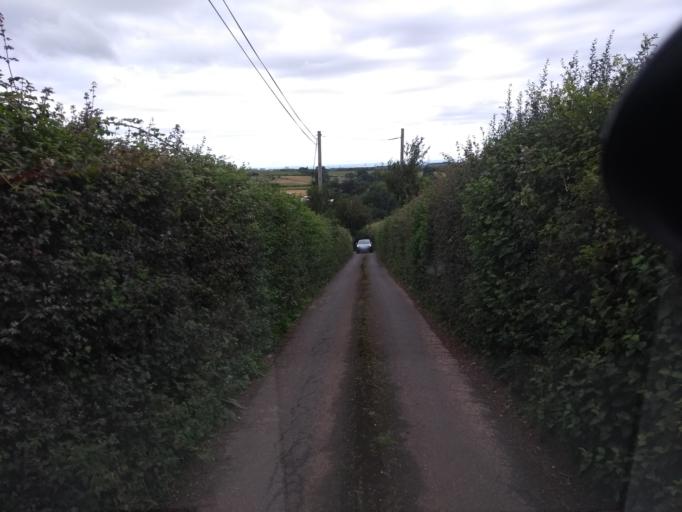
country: GB
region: England
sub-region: Somerset
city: Bridgwater
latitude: 51.1375
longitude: -3.0912
